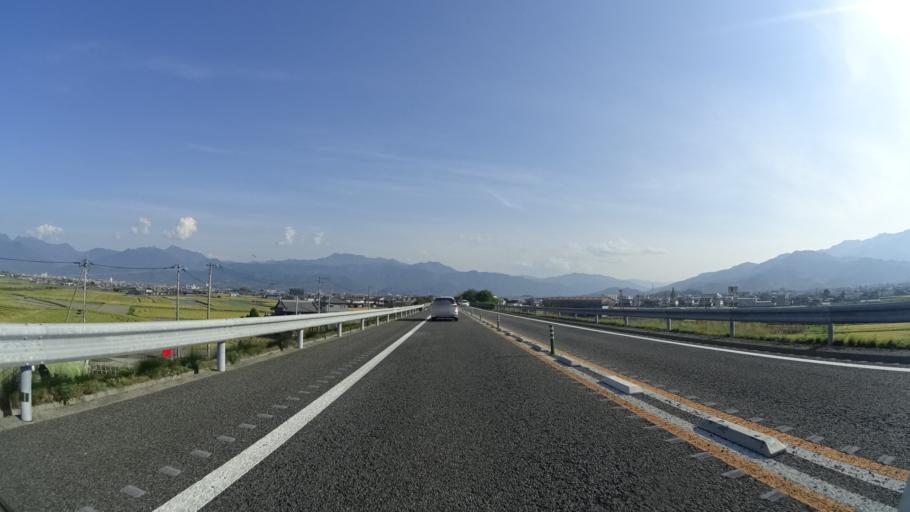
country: JP
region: Ehime
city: Saijo
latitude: 33.9466
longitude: 133.0691
